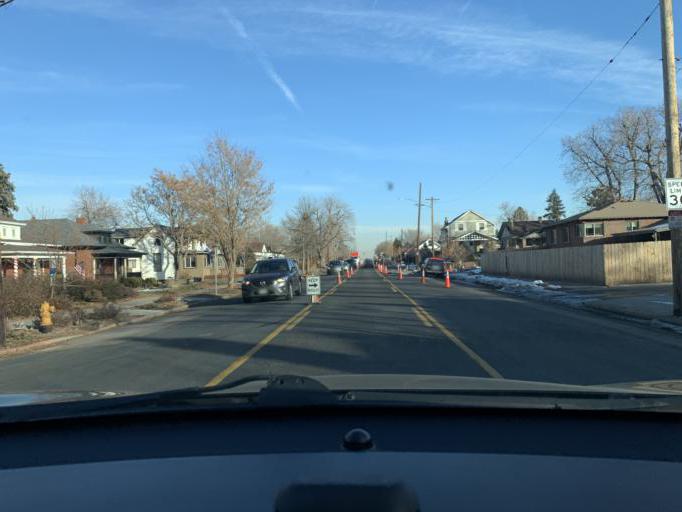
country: US
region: Colorado
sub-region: Adams County
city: Berkley
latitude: 39.7767
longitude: -105.0331
